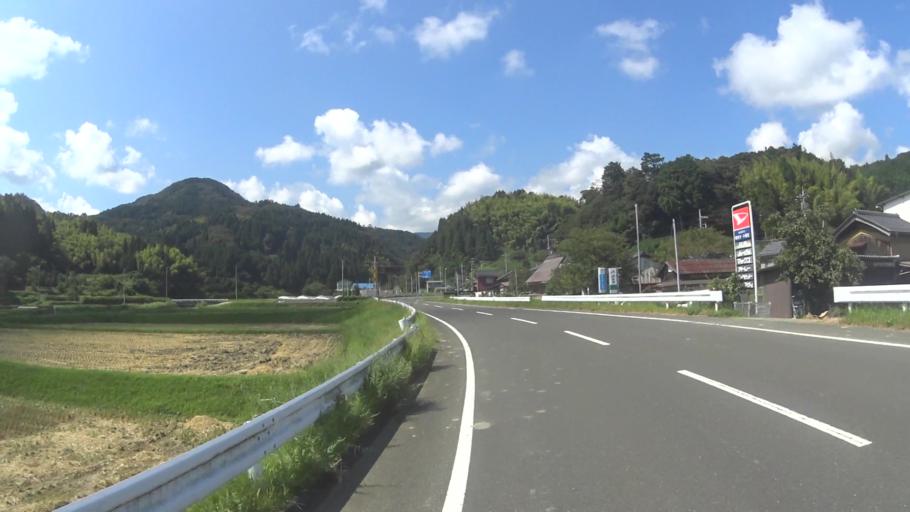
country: JP
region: Kyoto
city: Miyazu
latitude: 35.6572
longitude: 135.2585
